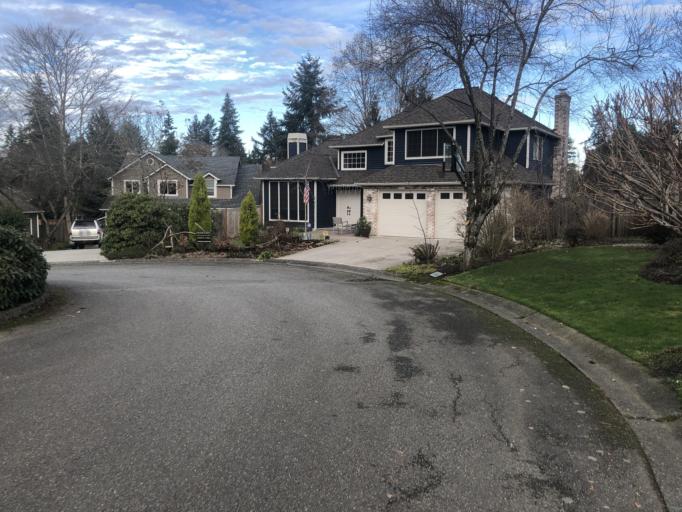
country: US
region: Washington
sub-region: King County
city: Redmond
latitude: 47.6906
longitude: -122.1033
